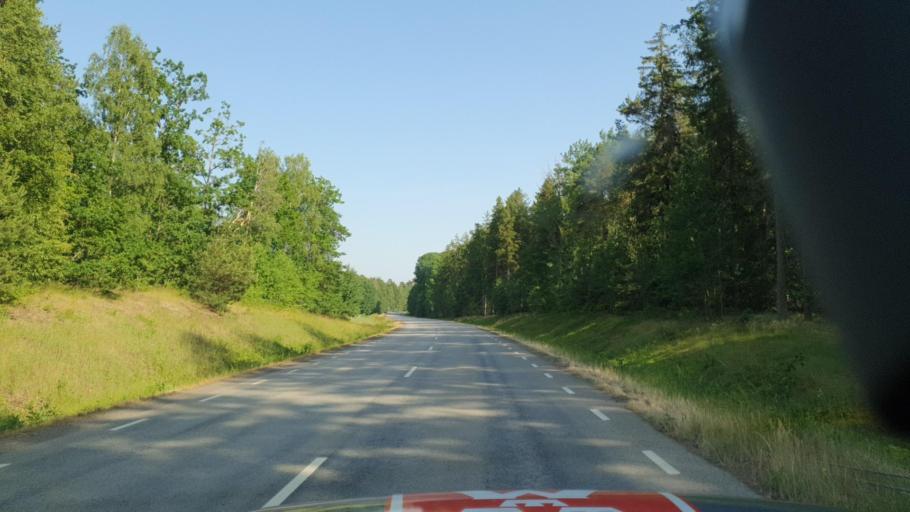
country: SE
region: Kalmar
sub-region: Kalmar Kommun
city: Ljungbyholm
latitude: 56.6419
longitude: 16.1732
